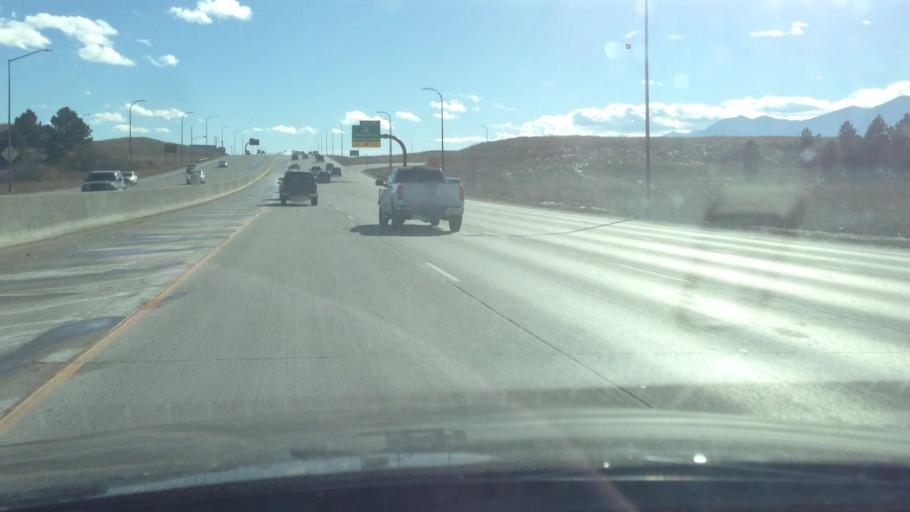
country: US
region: Colorado
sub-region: El Paso County
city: Monument
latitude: 39.0906
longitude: -104.8623
